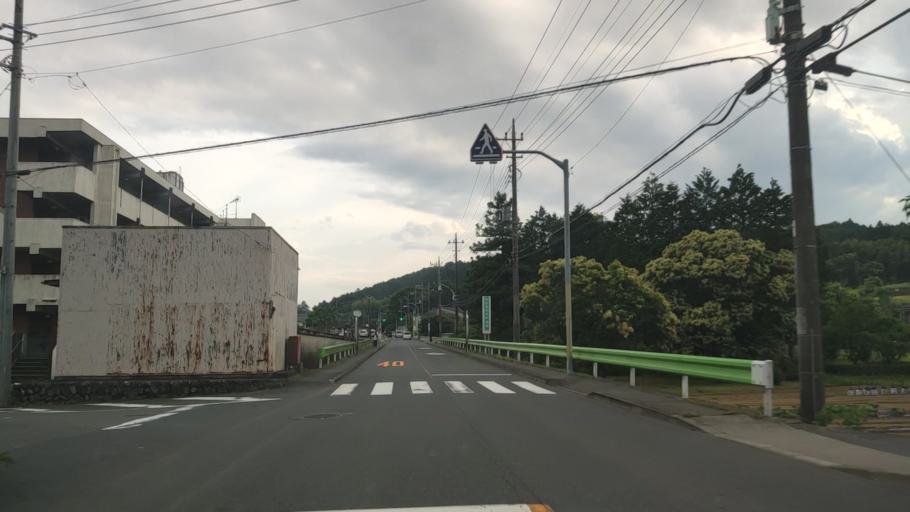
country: JP
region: Saitama
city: Hanno
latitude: 35.8292
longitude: 139.2935
